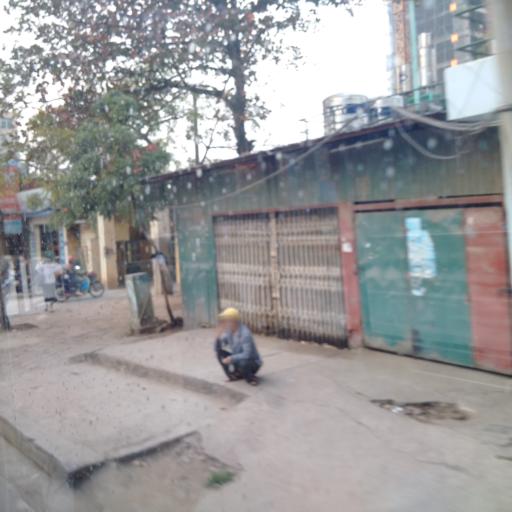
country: VN
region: Ha Noi
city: Cau Giay
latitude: 21.0461
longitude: 105.7981
